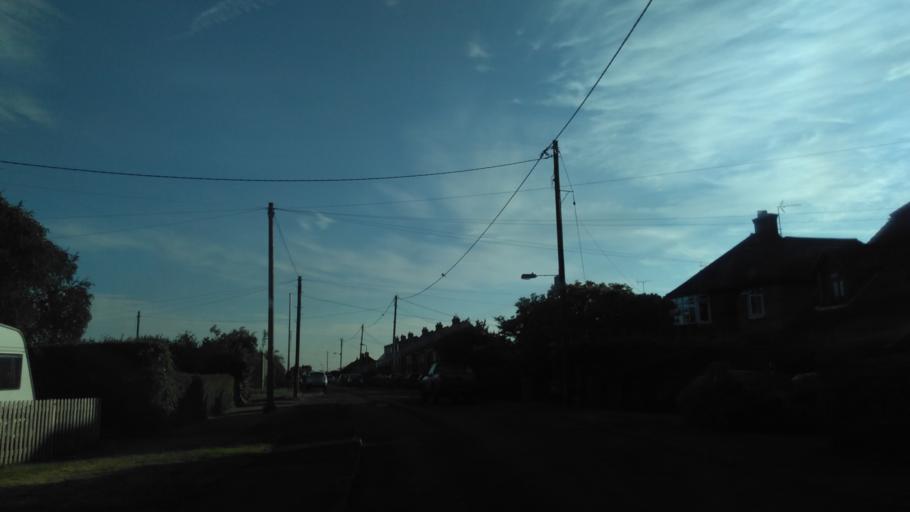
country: GB
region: England
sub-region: Kent
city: Dunkirk
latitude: 51.2919
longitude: 0.9796
